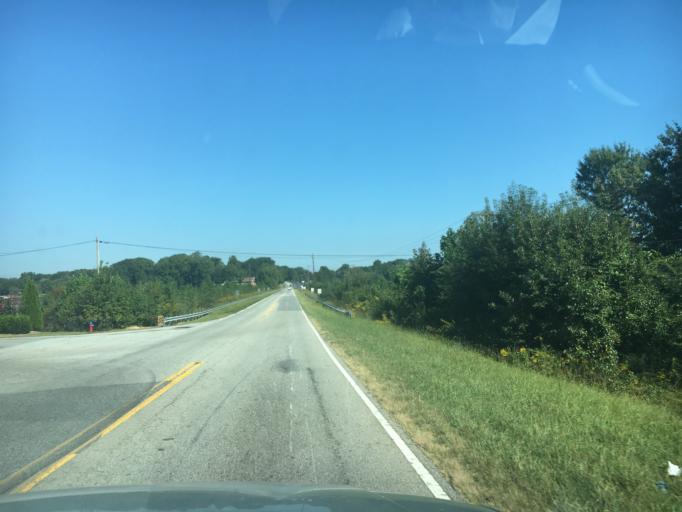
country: US
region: South Carolina
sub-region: Spartanburg County
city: Inman
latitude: 35.1097
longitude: -82.0403
